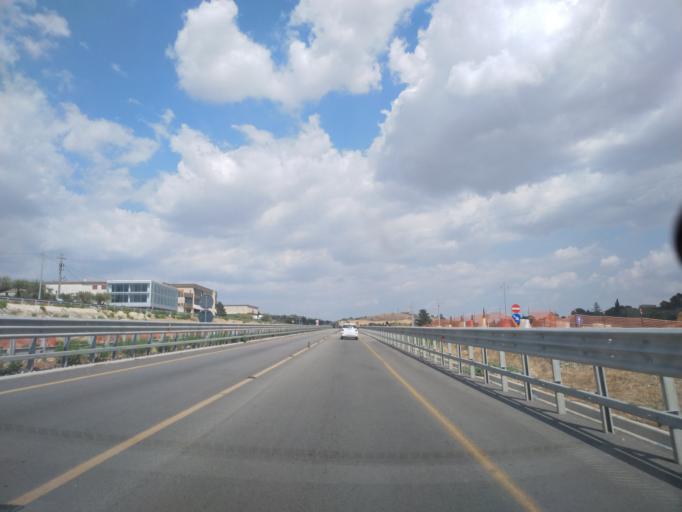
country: IT
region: Sicily
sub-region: Provincia di Caltanissetta
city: San Cataldo
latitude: 37.4523
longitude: 13.9773
